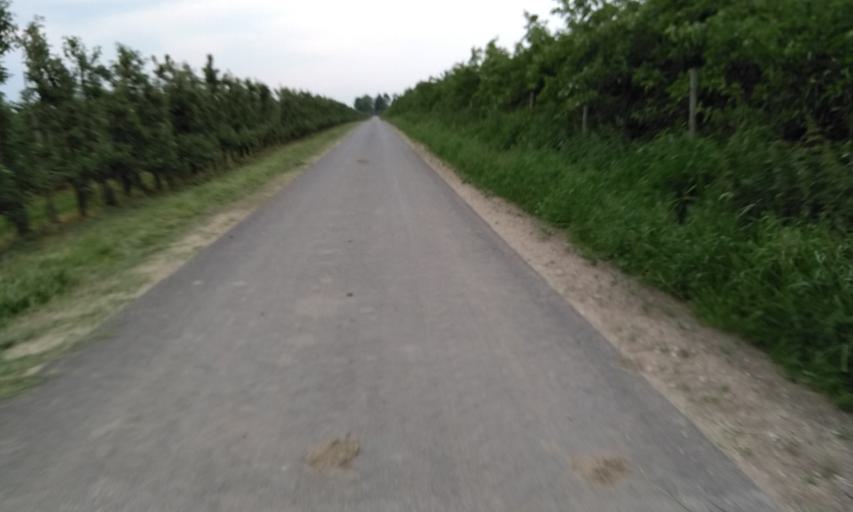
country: DE
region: Lower Saxony
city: Jork
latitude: 53.5089
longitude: 9.6881
